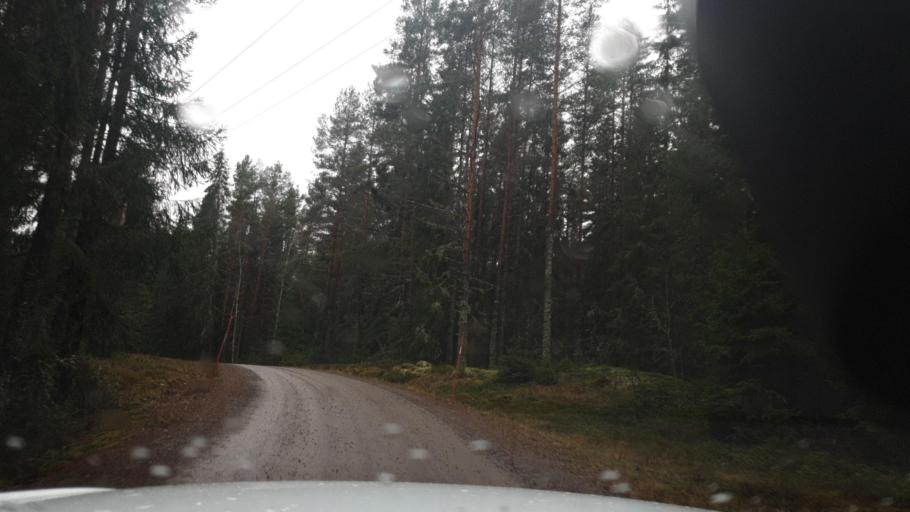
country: SE
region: Vaermland
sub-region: Grums Kommun
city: Grums
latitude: 59.5013
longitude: 12.9253
